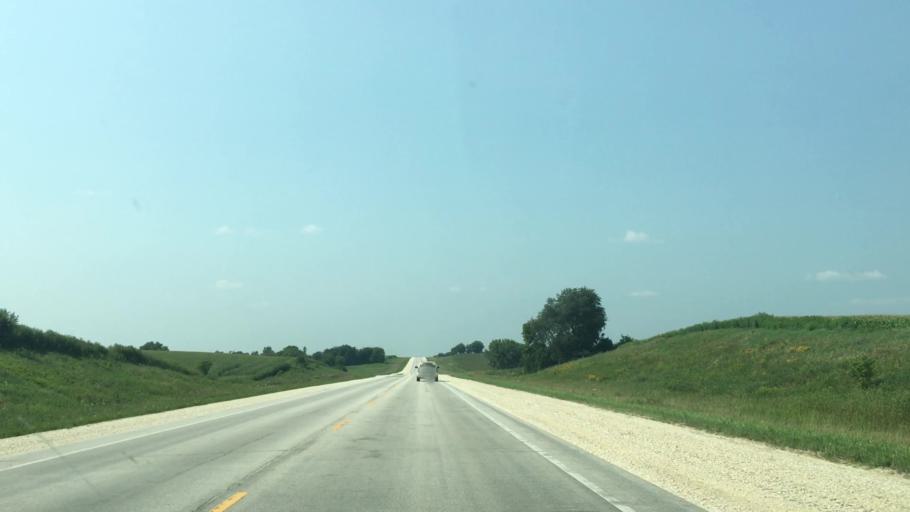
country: US
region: Iowa
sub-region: Winneshiek County
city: Decorah
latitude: 43.3747
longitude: -91.8137
